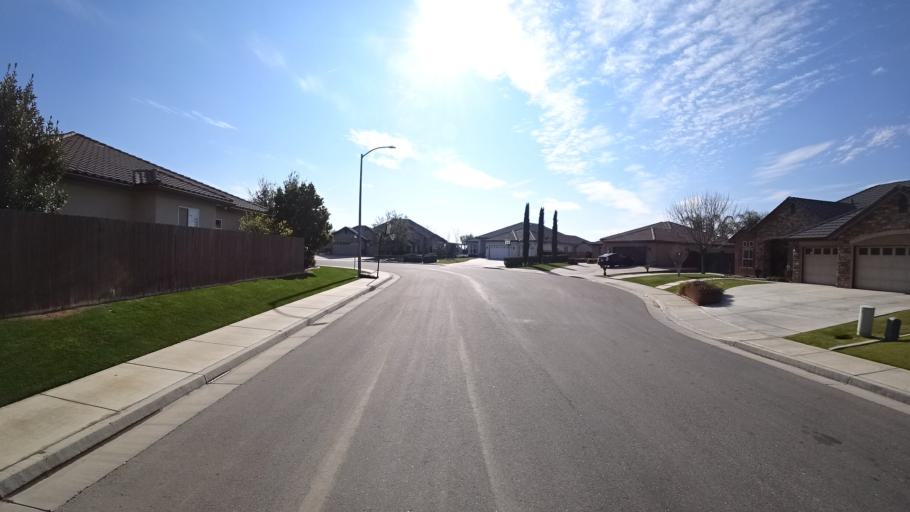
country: US
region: California
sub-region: Kern County
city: Lamont
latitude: 35.3880
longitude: -118.8837
